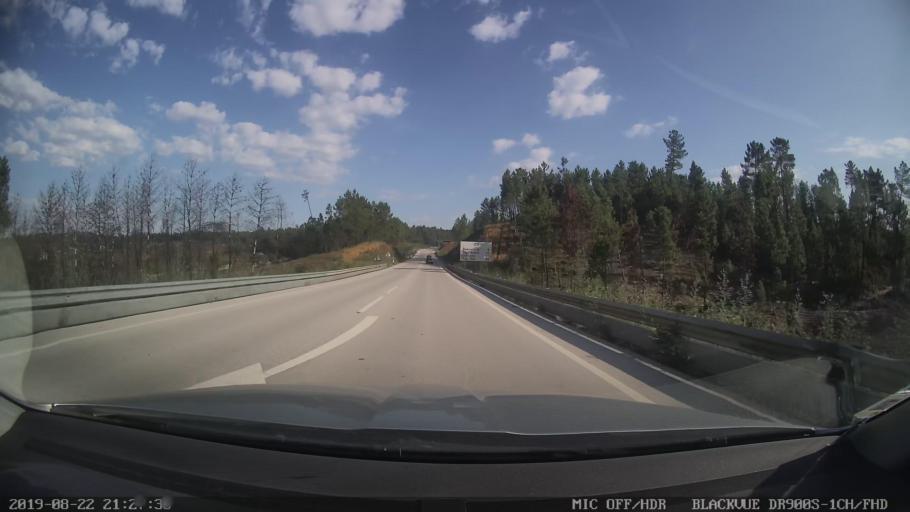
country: PT
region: Leiria
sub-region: Pedrogao Grande
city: Pedrogao Grande
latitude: 39.8792
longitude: -8.1188
